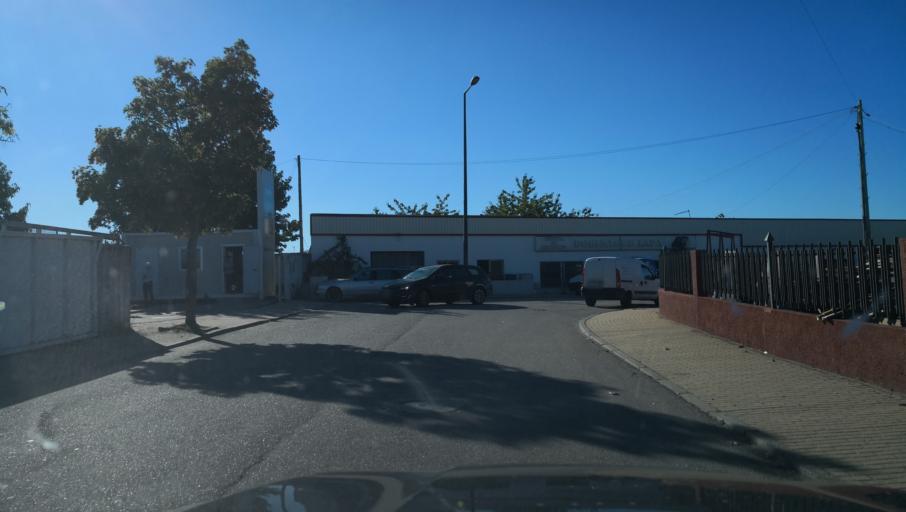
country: PT
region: Vila Real
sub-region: Vila Real
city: Vila Real
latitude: 41.2755
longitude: -7.7085
